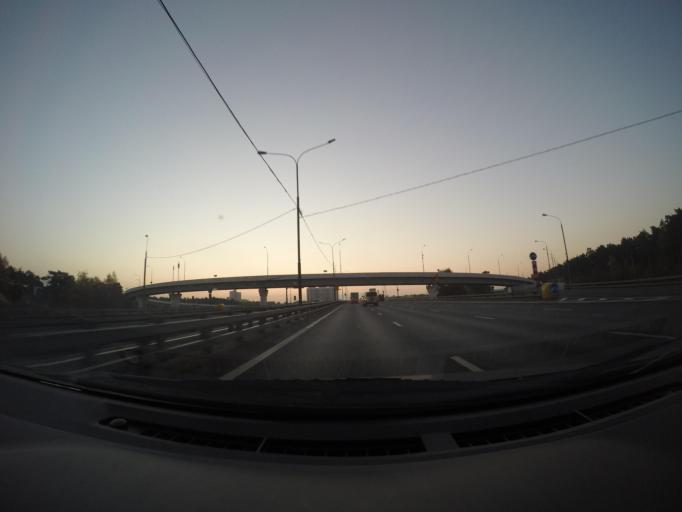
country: RU
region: Moscow
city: Vykhino-Zhulebino
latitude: 55.6888
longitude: 37.8262
